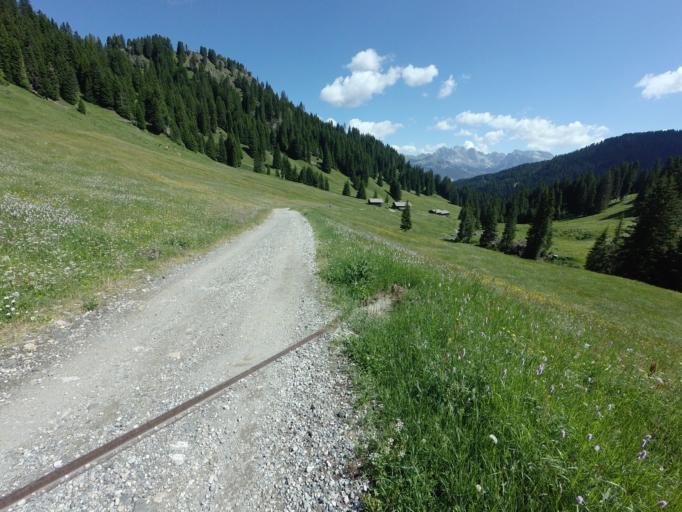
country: IT
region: Trentino-Alto Adige
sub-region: Bolzano
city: Ortisei
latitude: 46.5102
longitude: 11.6589
